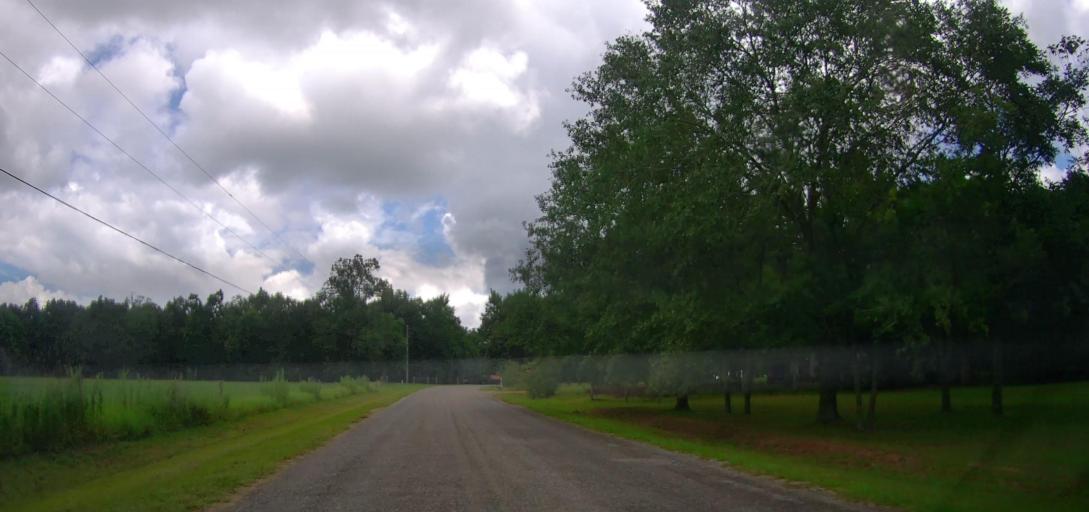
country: US
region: Georgia
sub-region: Pulaski County
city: Hawkinsville
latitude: 32.3174
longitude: -83.5328
